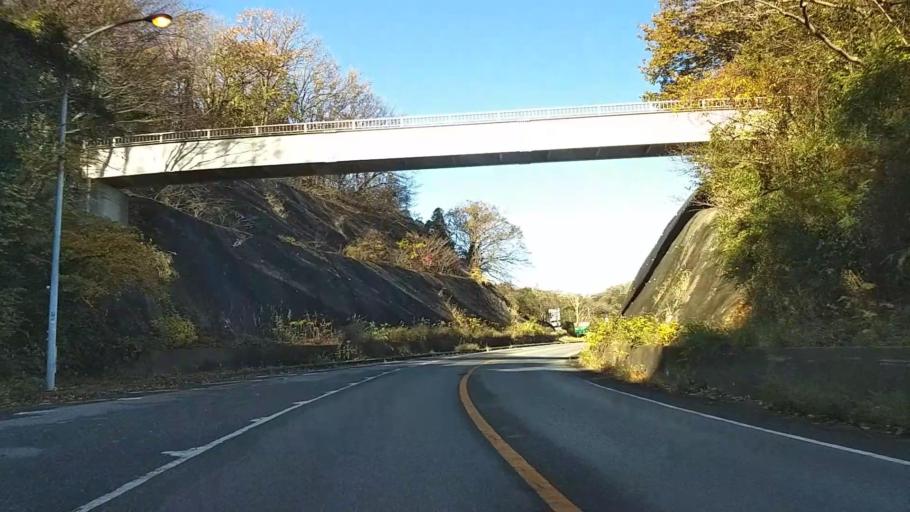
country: JP
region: Chiba
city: Futtsu
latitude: 35.2142
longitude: 139.8643
